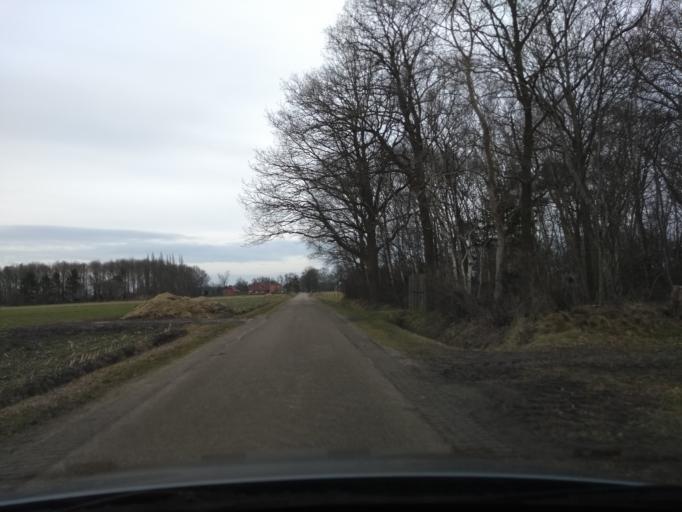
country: NL
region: Overijssel
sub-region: Gemeente Borne
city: Borne
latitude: 52.3475
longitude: 6.7339
